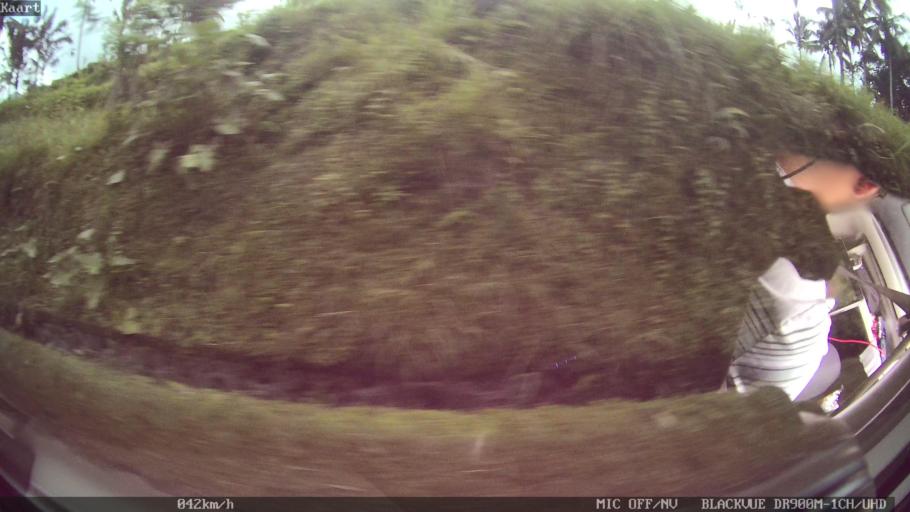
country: ID
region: Bali
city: Peneng
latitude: -8.3563
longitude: 115.2112
